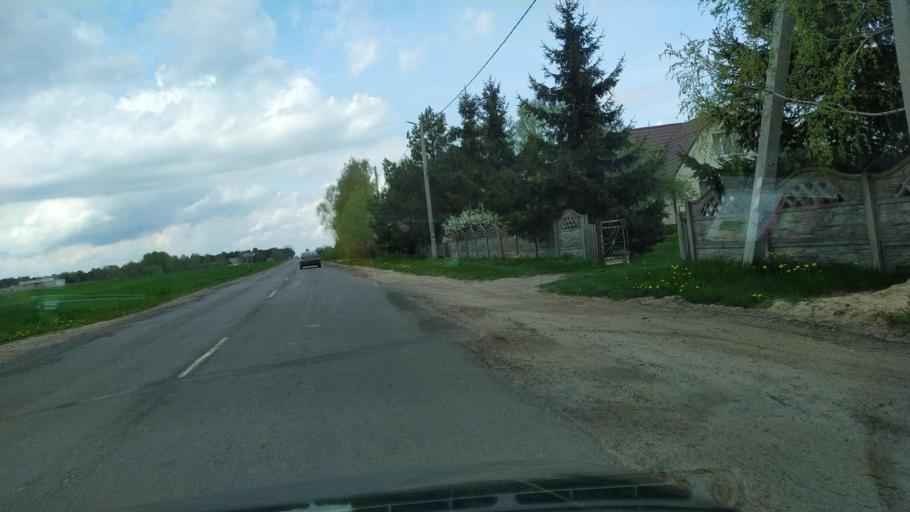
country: BY
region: Brest
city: Pruzhany
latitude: 52.5925
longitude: 24.4079
